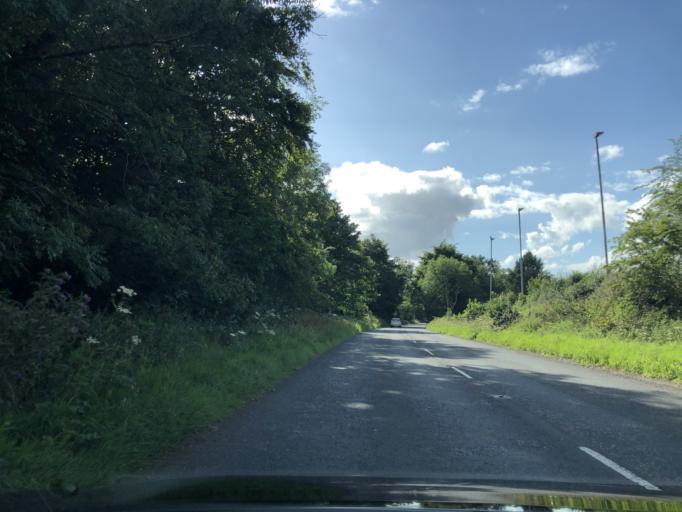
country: GB
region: Northern Ireland
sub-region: Ards District
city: Comber
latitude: 54.5472
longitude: -5.7448
